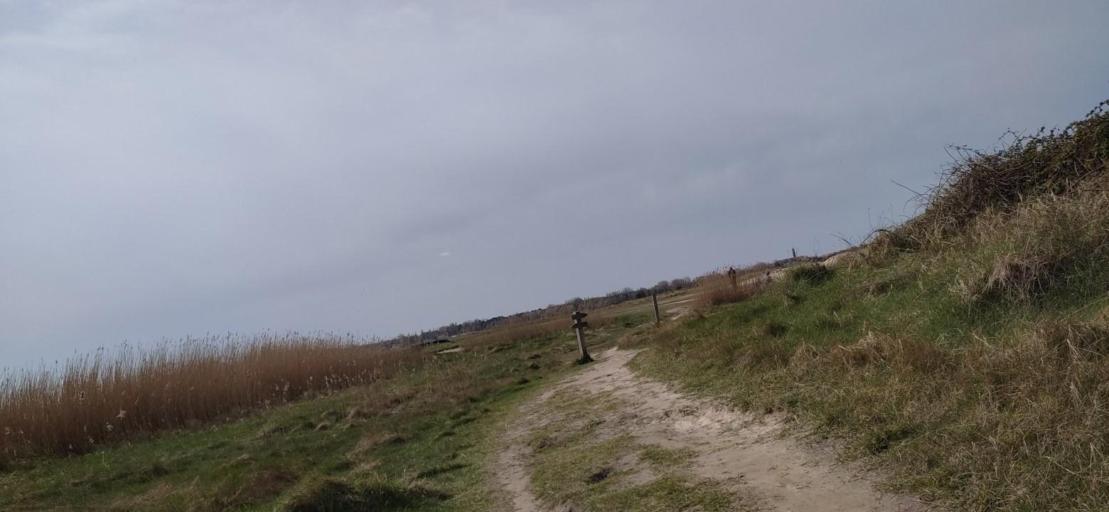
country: FR
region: Nord-Pas-de-Calais
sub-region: Departement du Pas-de-Calais
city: Etaples
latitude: 50.5380
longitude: 1.6103
